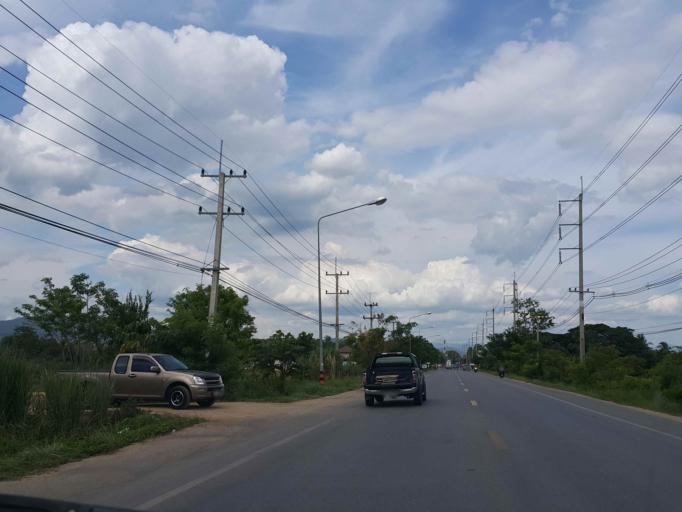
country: TH
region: Chiang Mai
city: San Sai
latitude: 18.9185
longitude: 98.9801
